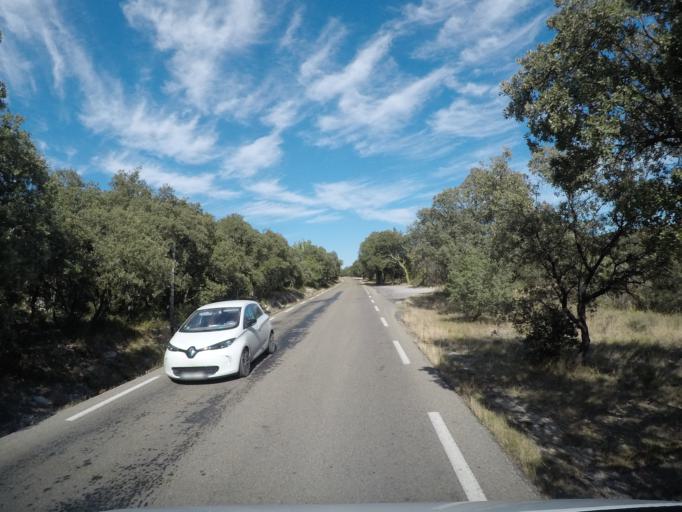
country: FR
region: Languedoc-Roussillon
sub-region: Departement du Gard
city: Anduze
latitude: 44.0016
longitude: 3.9785
